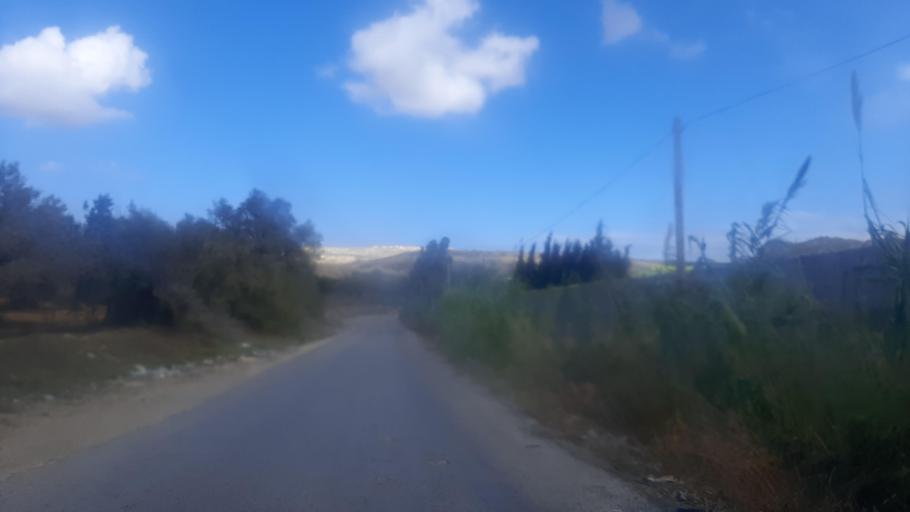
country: TN
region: Nabul
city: Nabeul
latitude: 36.4889
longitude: 10.6991
